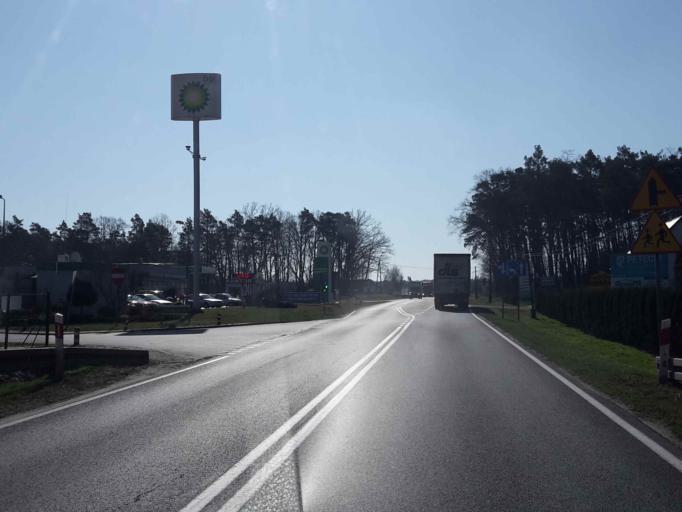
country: PL
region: Greater Poland Voivodeship
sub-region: Powiat nowotomyski
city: Nowy Tomysl
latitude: 52.3398
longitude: 16.1075
